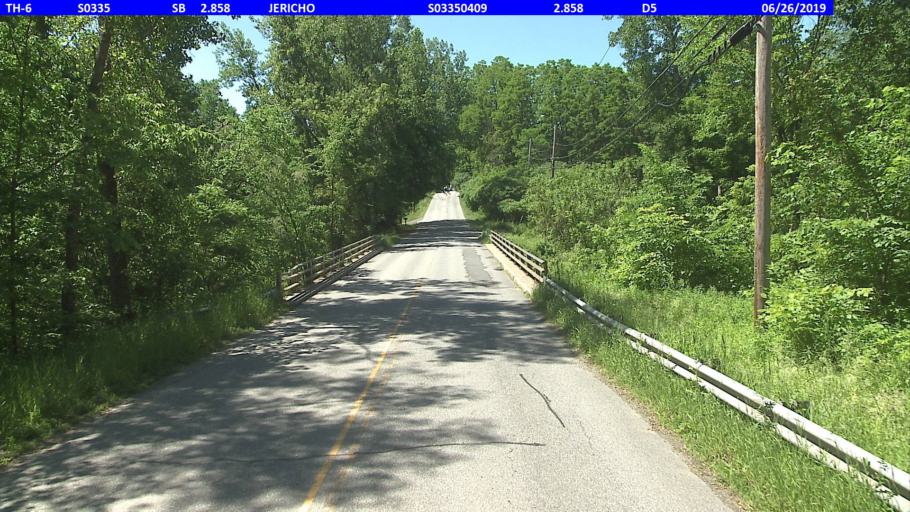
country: US
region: Vermont
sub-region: Chittenden County
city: Jericho
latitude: 44.5003
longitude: -72.9978
